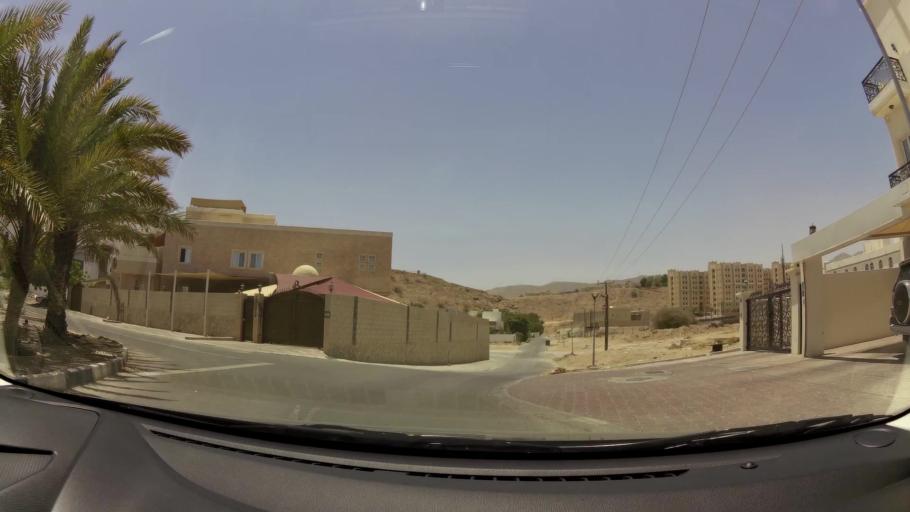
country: OM
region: Muhafazat Masqat
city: Bawshar
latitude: 23.6045
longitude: 58.4634
